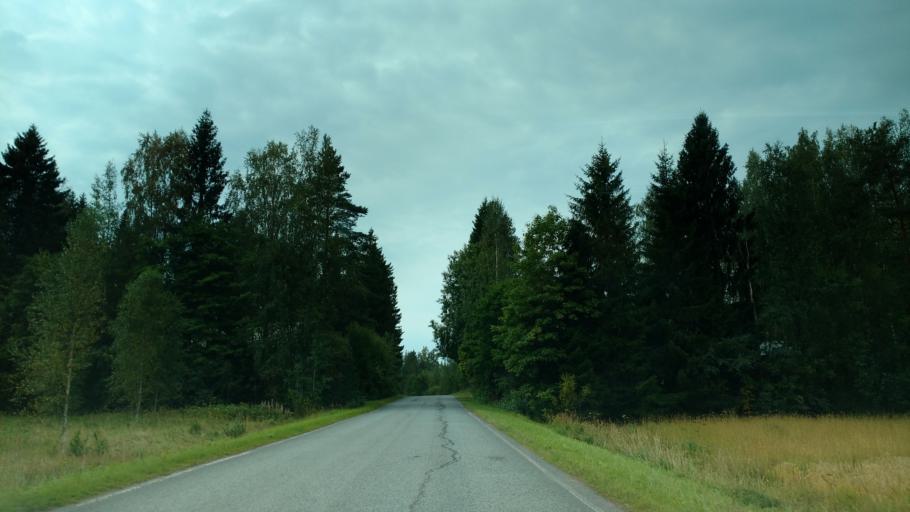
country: FI
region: Haeme
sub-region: Forssa
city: Ypaejae
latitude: 60.7617
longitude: 23.2129
